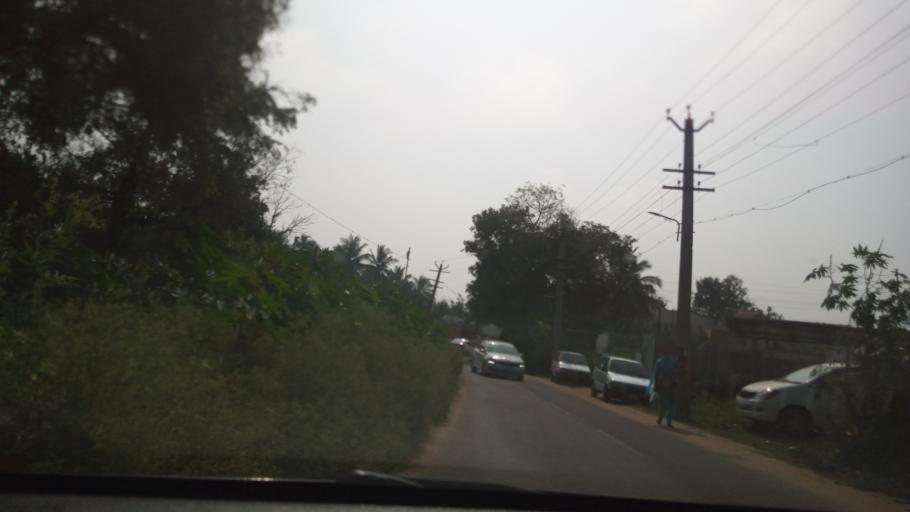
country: IN
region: Tamil Nadu
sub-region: Coimbatore
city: Perur
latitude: 11.0057
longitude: 76.8889
